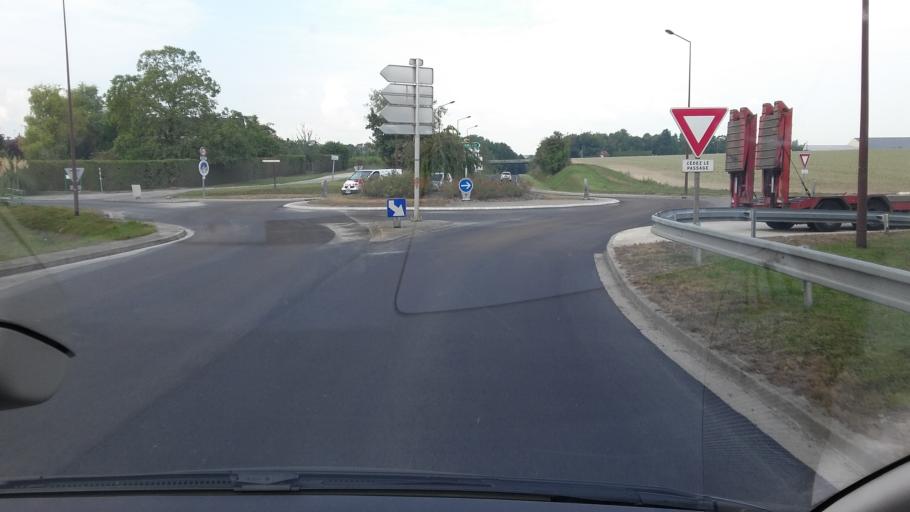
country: FR
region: Champagne-Ardenne
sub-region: Departement de la Marne
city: Fere-Champenoise
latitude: 48.7531
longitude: 4.0004
